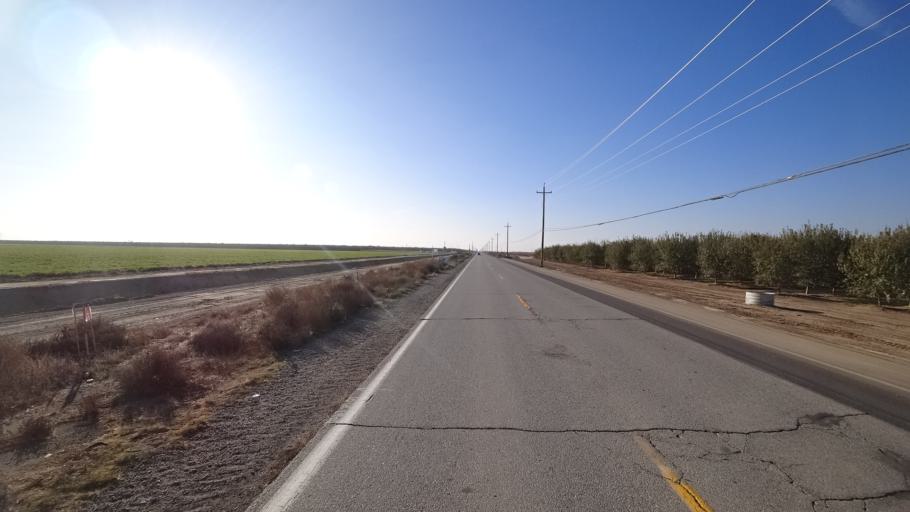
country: US
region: California
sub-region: Kern County
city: Rosedale
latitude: 35.2962
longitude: -119.1426
